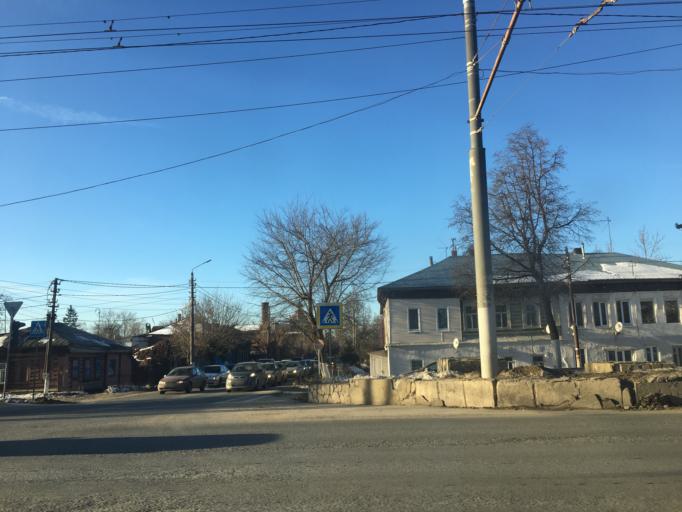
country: RU
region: Tula
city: Tula
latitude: 54.1978
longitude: 37.6343
